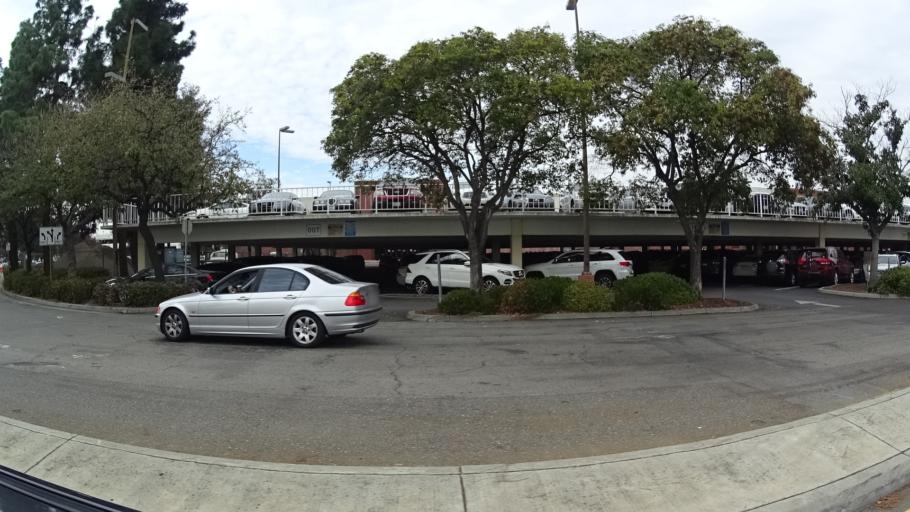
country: US
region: California
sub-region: Santa Clara County
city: Burbank
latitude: 37.3239
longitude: -121.9423
